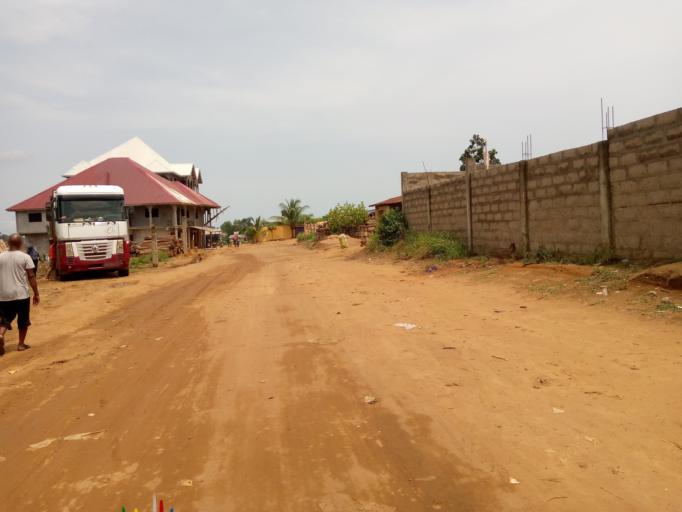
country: SL
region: Western Area
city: Waterloo
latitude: 8.3329
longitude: -13.0294
